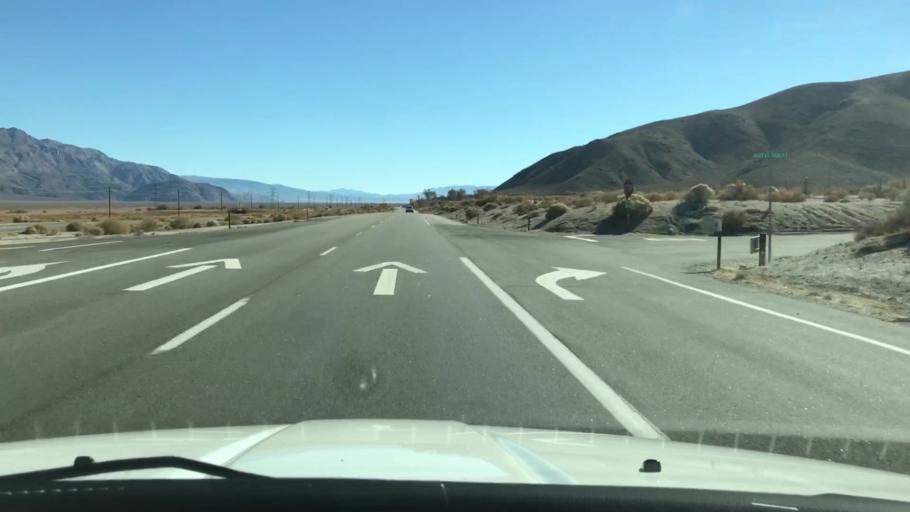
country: US
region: California
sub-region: Inyo County
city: Lone Pine
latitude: 36.6841
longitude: -118.1060
